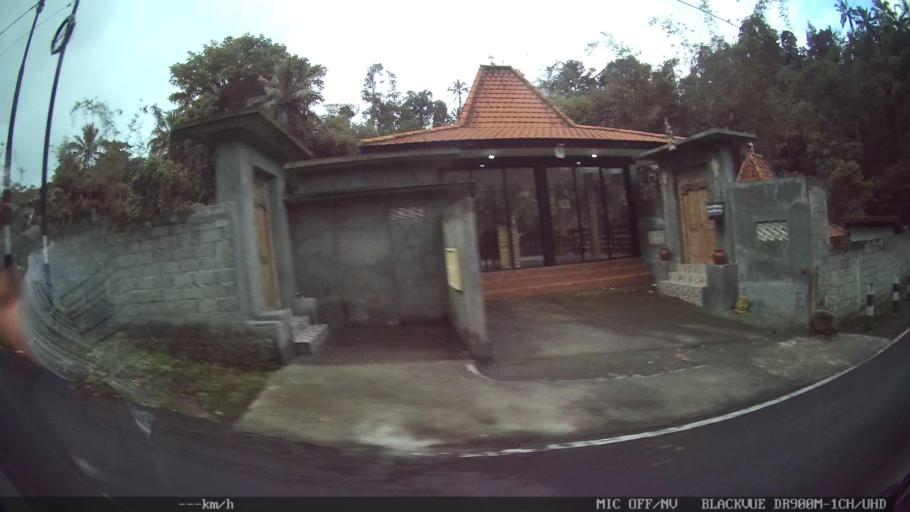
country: ID
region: Bali
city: Peneng
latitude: -8.3628
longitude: 115.1801
